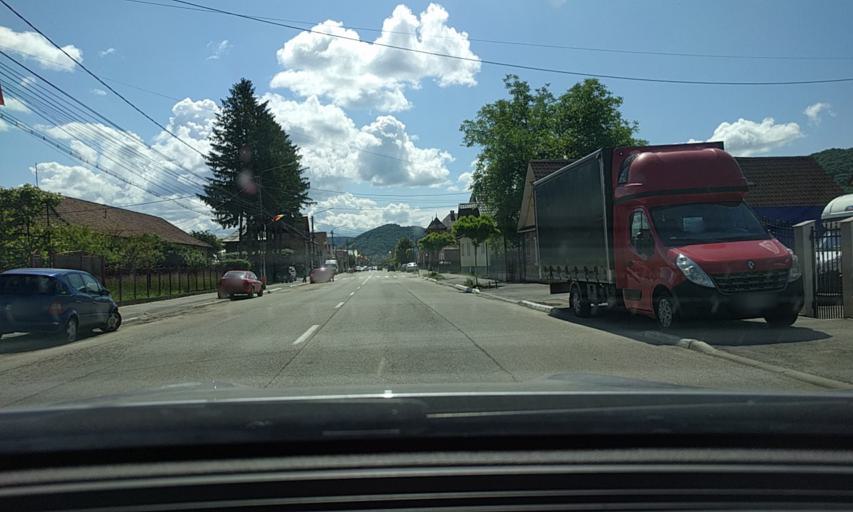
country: RO
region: Bistrita-Nasaud
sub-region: Oras Nasaud
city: Nasaud
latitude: 47.2924
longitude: 24.3873
